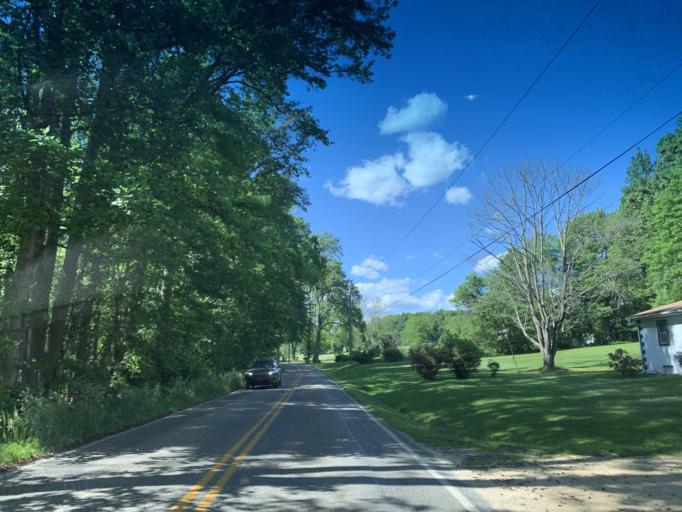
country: US
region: Maryland
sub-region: Cecil County
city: North East
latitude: 39.5435
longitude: -75.9178
